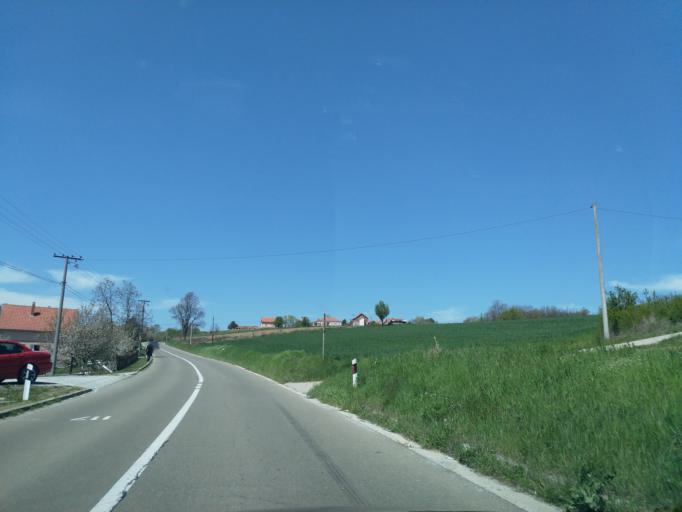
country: RS
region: Central Serbia
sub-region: Belgrade
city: Lazarevac
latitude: 44.3644
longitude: 20.3485
